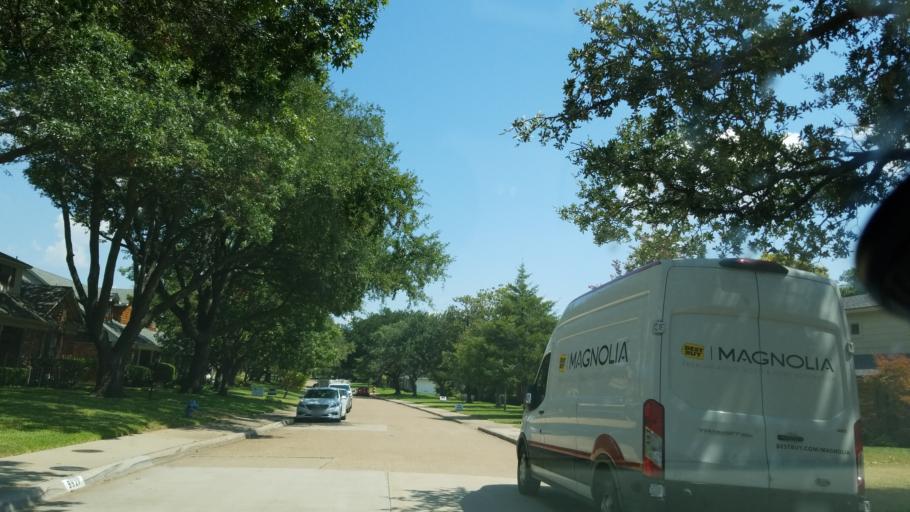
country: US
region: Texas
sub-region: Dallas County
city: Richardson
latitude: 32.8897
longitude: -96.7153
